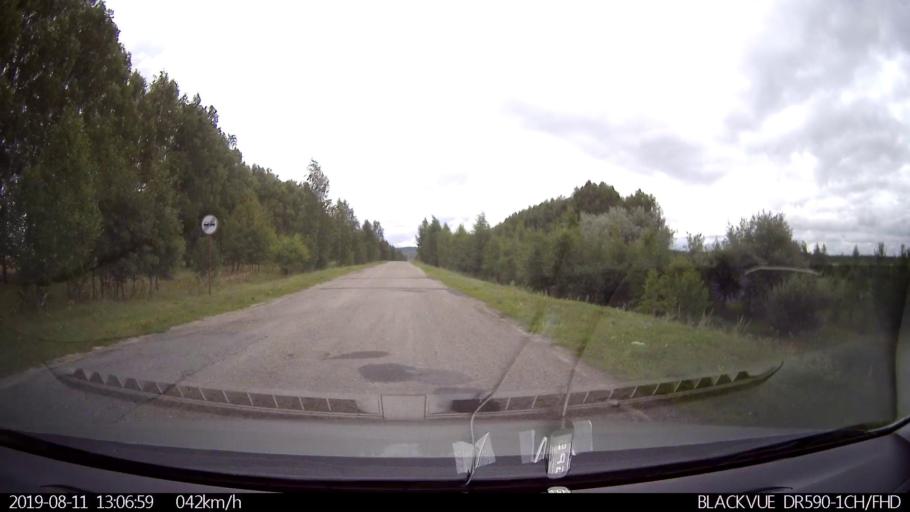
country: RU
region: Ulyanovsk
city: Ignatovka
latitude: 53.8661
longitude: 47.6394
